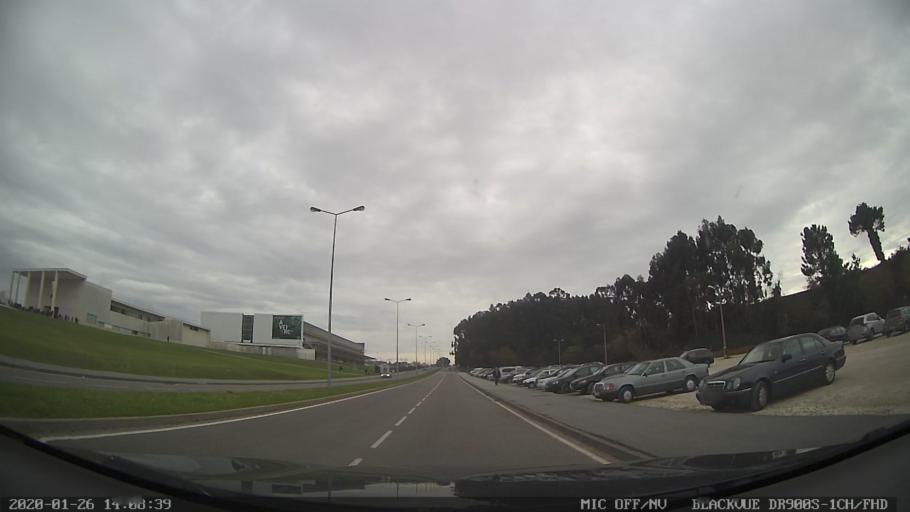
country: PT
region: Aveiro
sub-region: Aveiro
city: Aveiro
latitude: 40.6345
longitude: -8.6341
